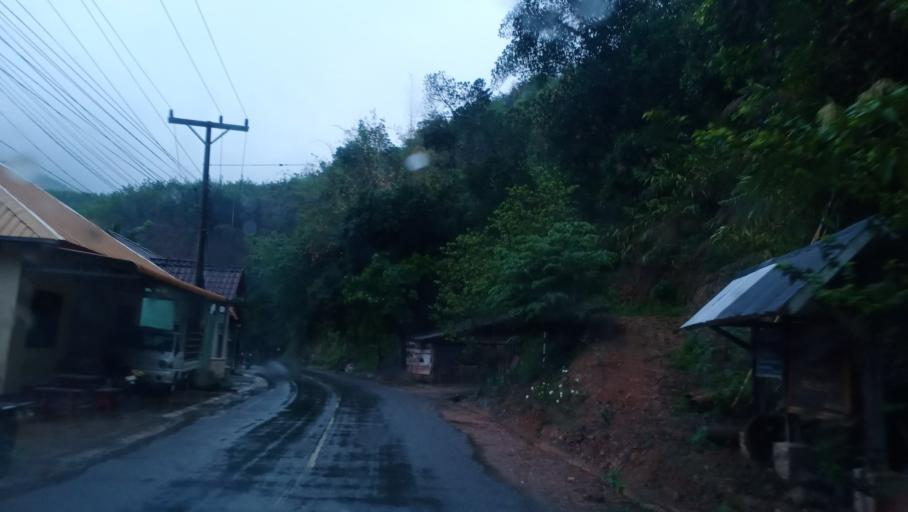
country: LA
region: Phongsali
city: Khoa
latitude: 21.0786
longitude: 102.5008
